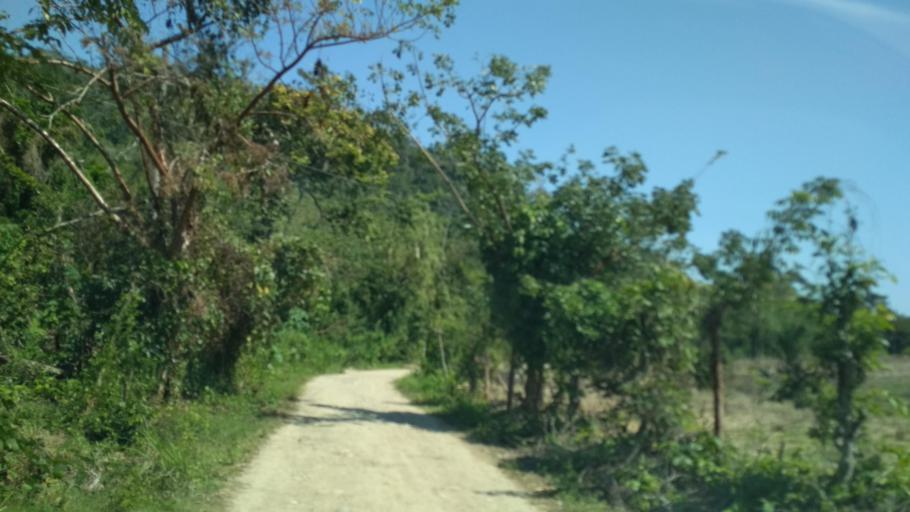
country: MX
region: Veracruz
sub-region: Papantla
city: Polutla
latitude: 20.4823
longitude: -97.2256
